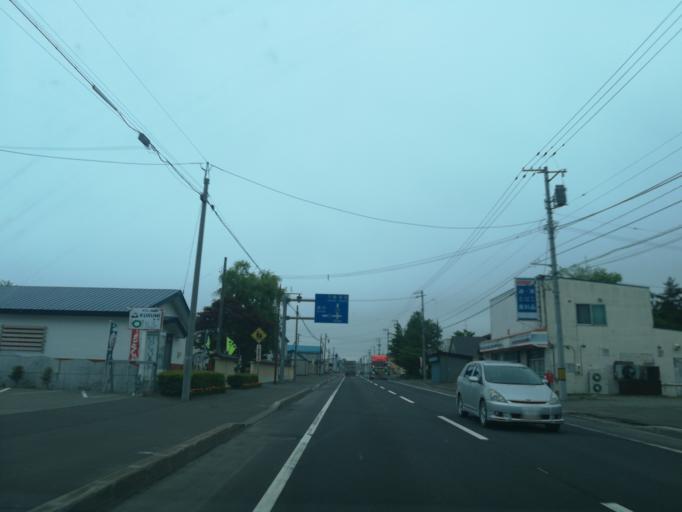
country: JP
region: Hokkaido
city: Ebetsu
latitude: 43.0711
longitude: 141.6481
